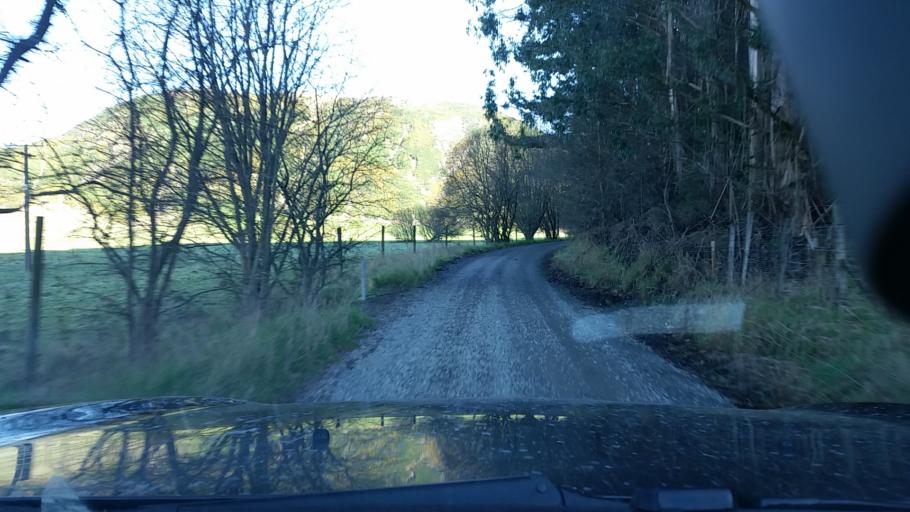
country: NZ
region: Marlborough
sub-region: Marlborough District
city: Blenheim
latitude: -41.4632
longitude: 173.7960
